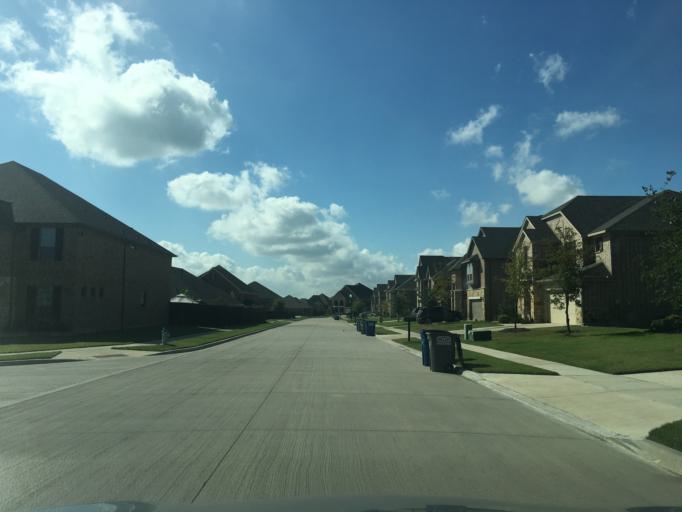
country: US
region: Texas
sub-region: Dallas County
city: Sachse
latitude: 32.9632
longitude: -96.5746
